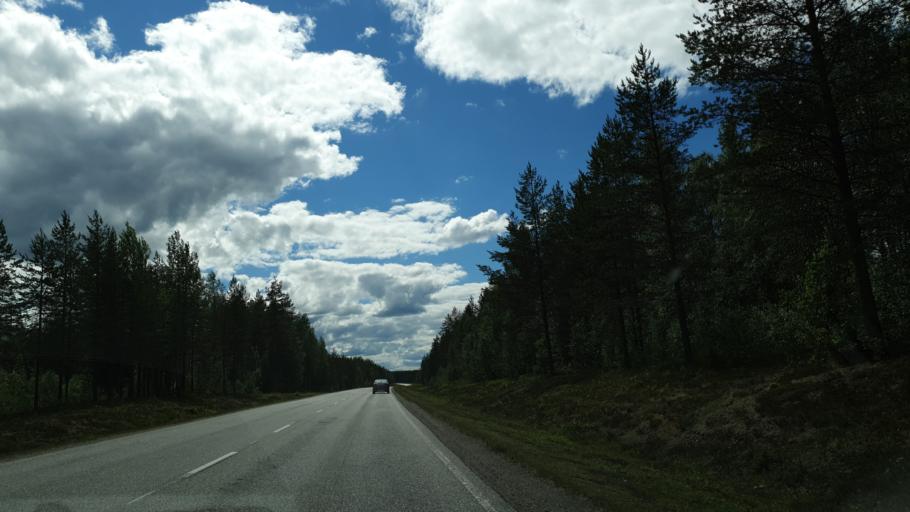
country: FI
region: North Karelia
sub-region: Pielisen Karjala
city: Valtimo
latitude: 63.4517
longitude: 28.7955
